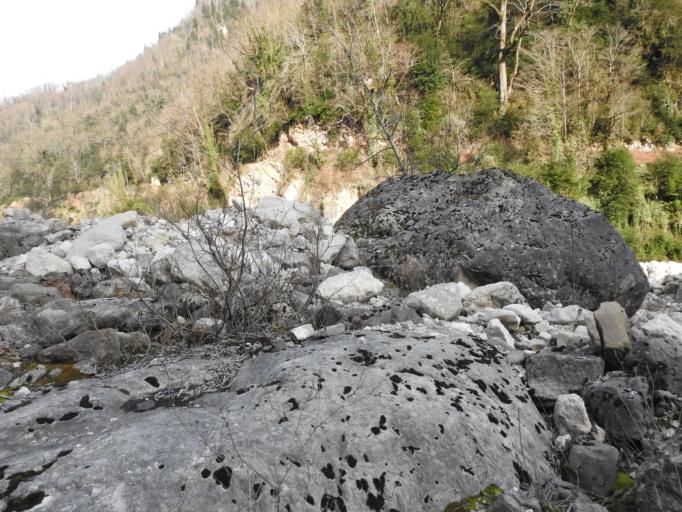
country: GE
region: Abkhazia
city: Gudauta
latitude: 43.2512
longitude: 40.6578
